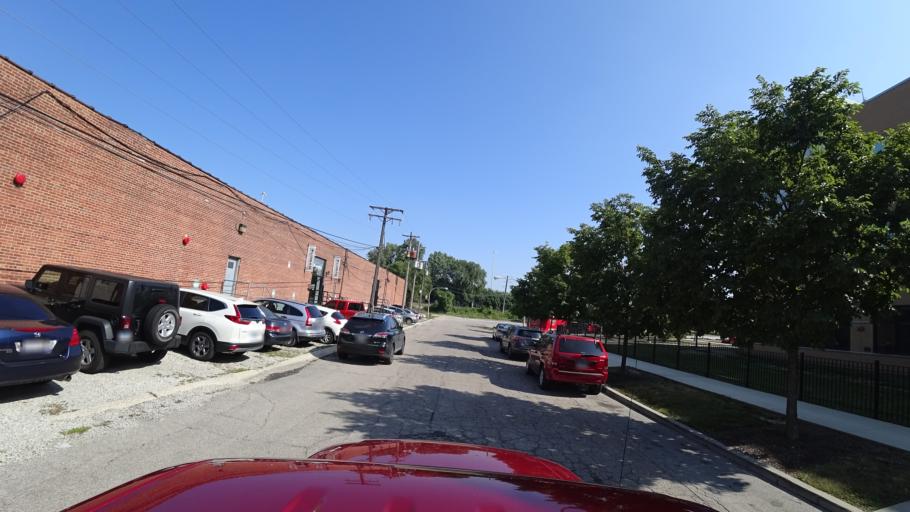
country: US
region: Illinois
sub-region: Cook County
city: Cicero
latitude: 41.8252
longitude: -87.7118
